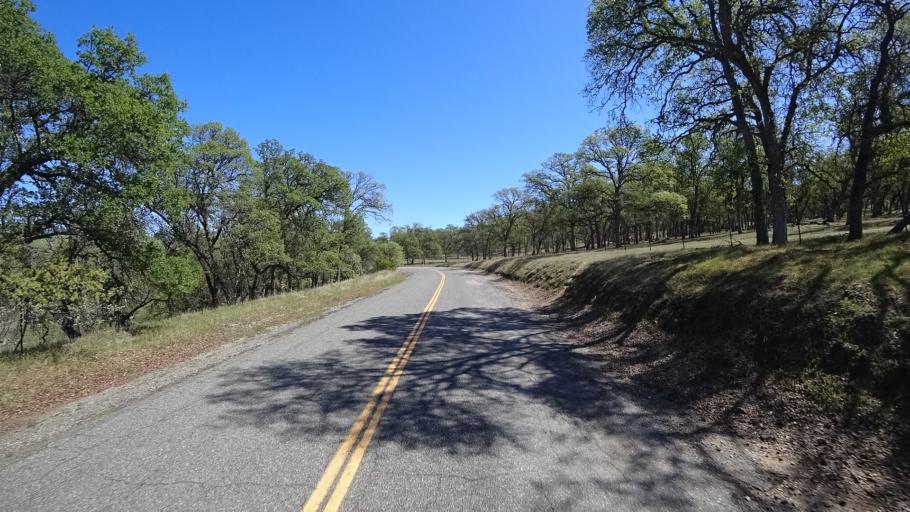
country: US
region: California
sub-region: Glenn County
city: Orland
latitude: 39.7365
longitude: -122.3939
